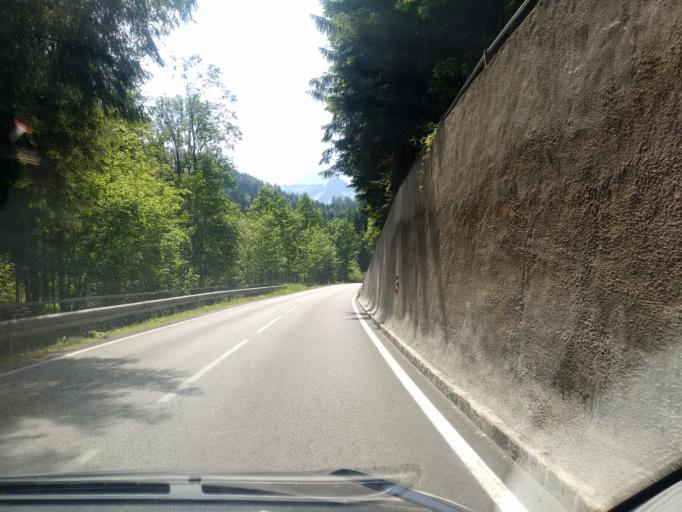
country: AT
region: Upper Austria
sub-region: Politischer Bezirk Kirchdorf an der Krems
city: Rossleithen
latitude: 47.7072
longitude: 14.1976
